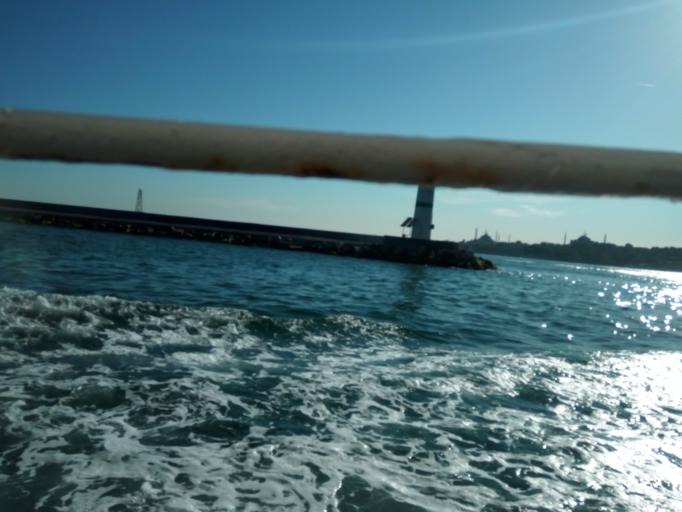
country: TR
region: Istanbul
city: UEskuedar
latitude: 41.0095
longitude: 29.0028
